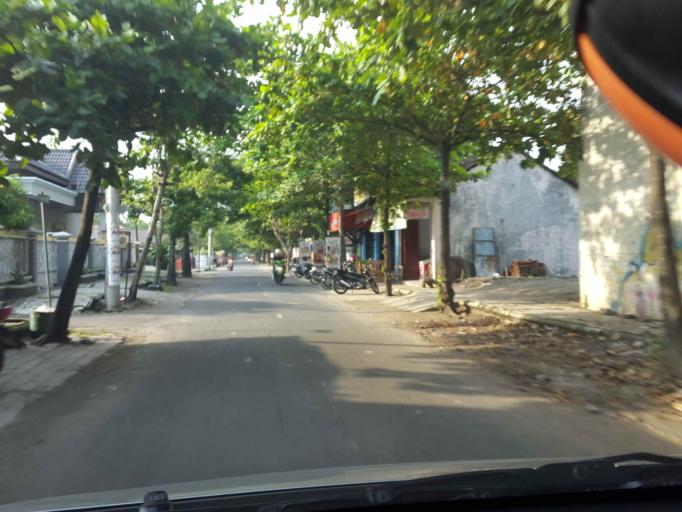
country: ID
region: Central Java
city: Sragen
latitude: -7.4294
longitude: 111.0114
